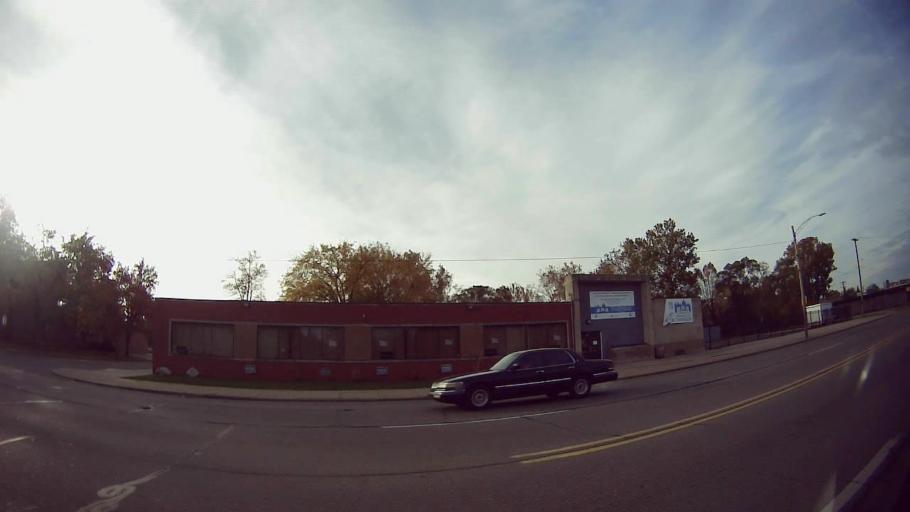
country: US
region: Michigan
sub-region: Oakland County
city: Oak Park
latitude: 42.4302
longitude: -83.2130
